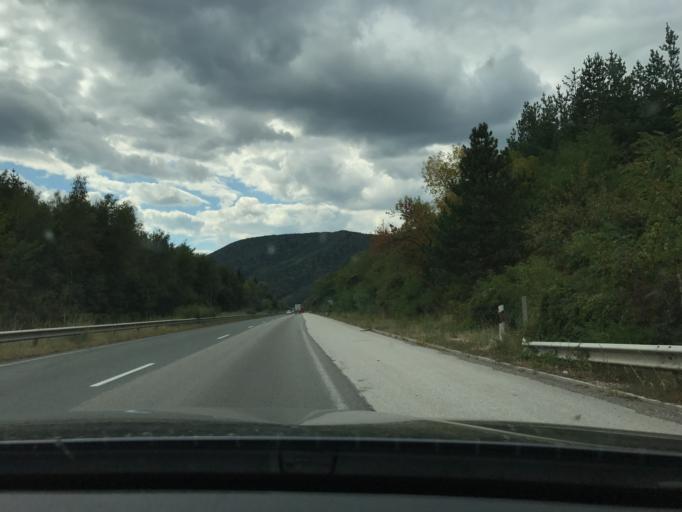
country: BG
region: Sofiya
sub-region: Obshtina Botevgrad
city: Botevgrad
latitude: 42.8855
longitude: 23.8150
